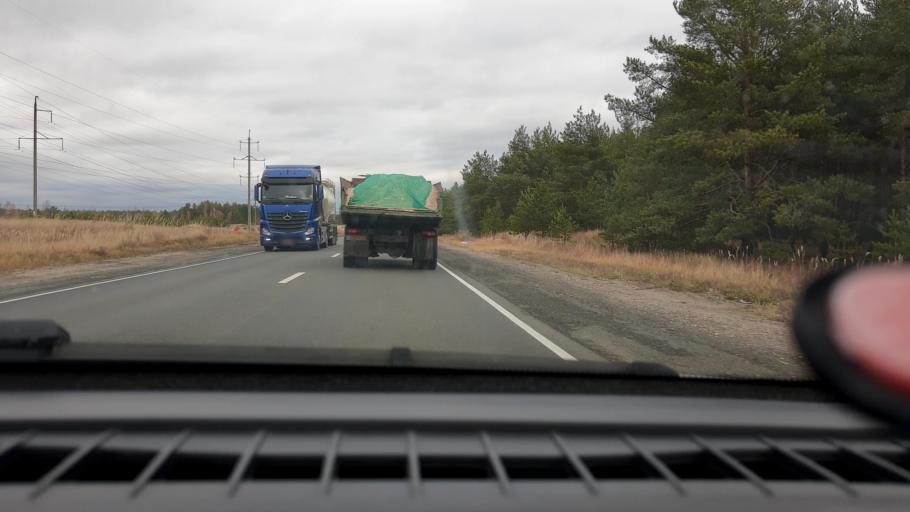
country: RU
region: Nizjnij Novgorod
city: Lukino
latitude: 56.3806
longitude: 43.6307
